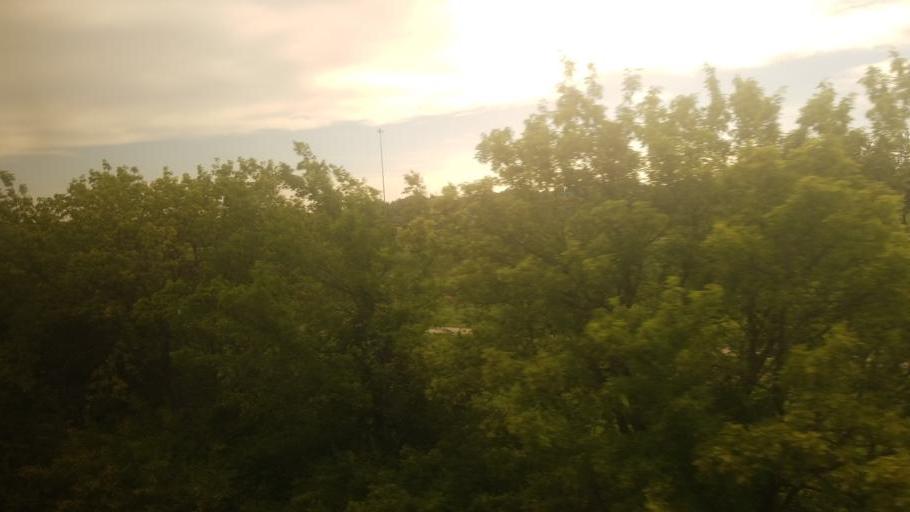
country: US
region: Kansas
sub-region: Shawnee County
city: Topeka
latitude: 39.0387
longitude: -95.6700
